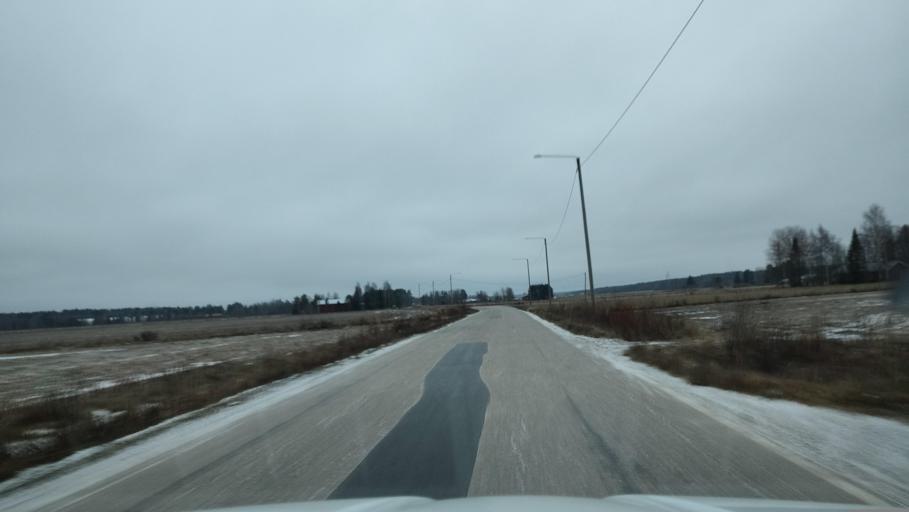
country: FI
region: Southern Ostrobothnia
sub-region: Suupohja
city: Karijoki
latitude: 62.2624
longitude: 21.6823
